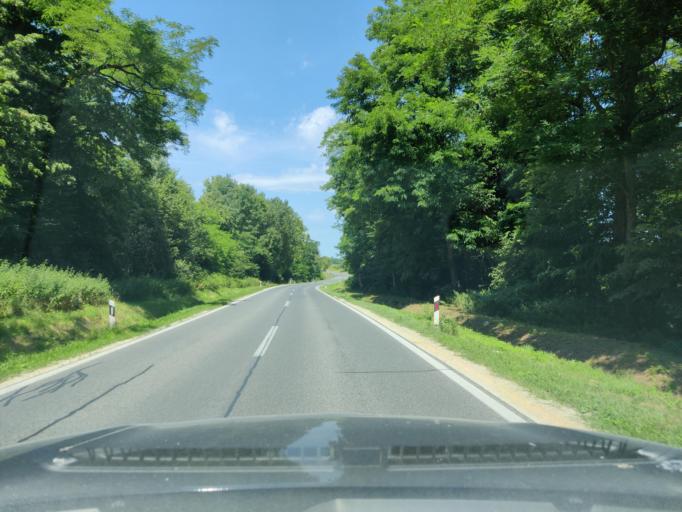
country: HR
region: Medimurska
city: Mackovec
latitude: 46.4556
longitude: 16.4311
